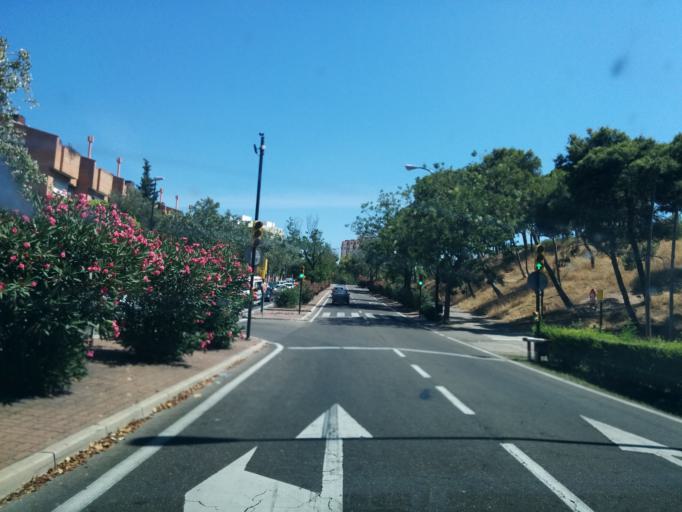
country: ES
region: Aragon
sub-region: Provincia de Zaragoza
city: Delicias
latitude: 41.6348
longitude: -0.8929
